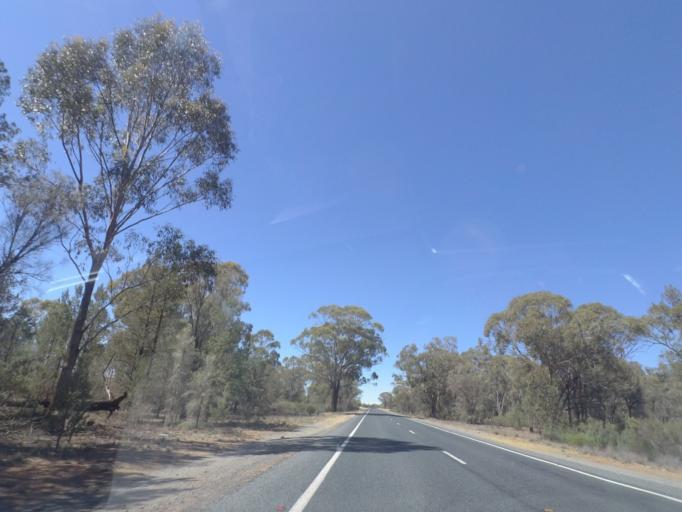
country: AU
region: New South Wales
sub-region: Narrandera
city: Narrandera
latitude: -34.4430
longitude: 146.8407
